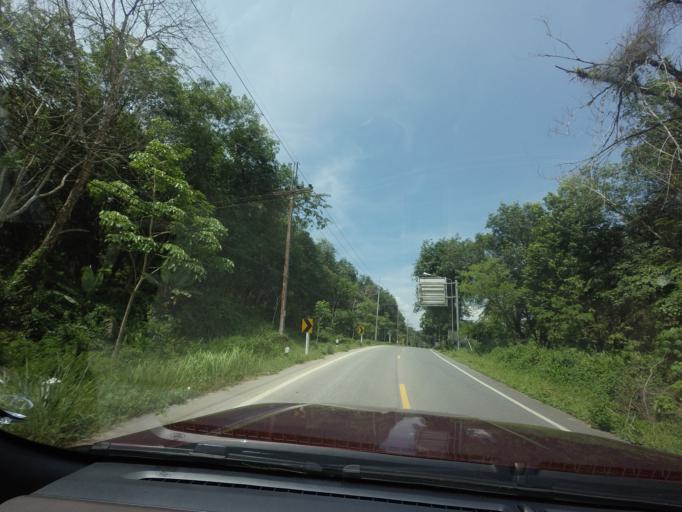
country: TH
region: Yala
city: Betong
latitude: 5.8462
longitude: 101.0746
